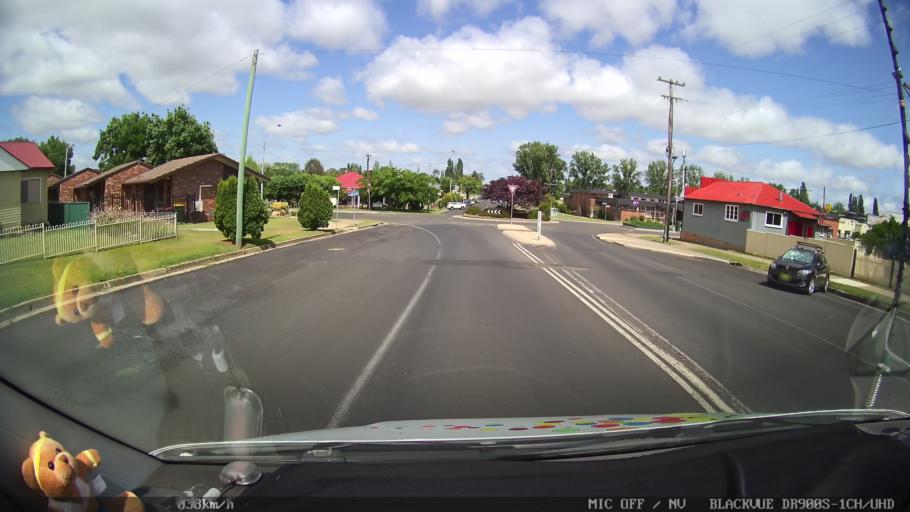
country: AU
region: New South Wales
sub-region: Glen Innes Severn
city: Glen Innes
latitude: -29.7433
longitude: 151.7355
